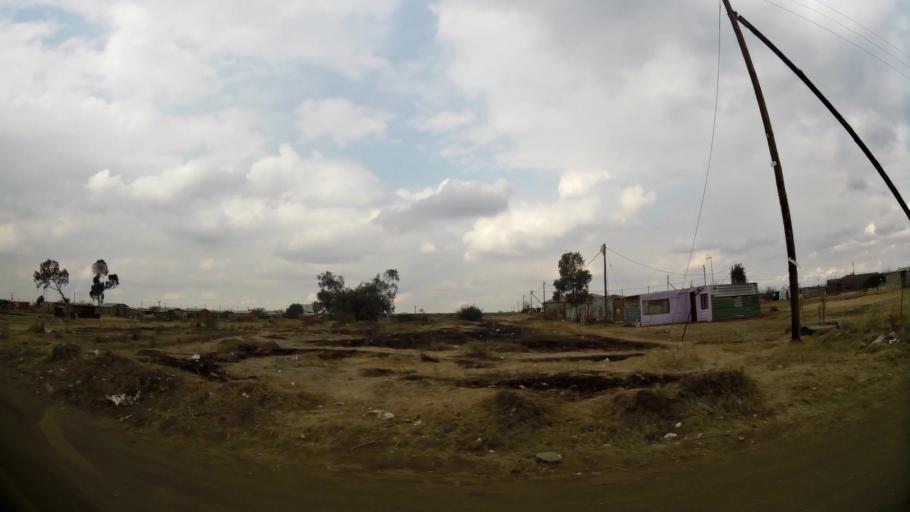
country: ZA
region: Orange Free State
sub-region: Fezile Dabi District Municipality
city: Sasolburg
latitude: -26.8624
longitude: 27.8805
